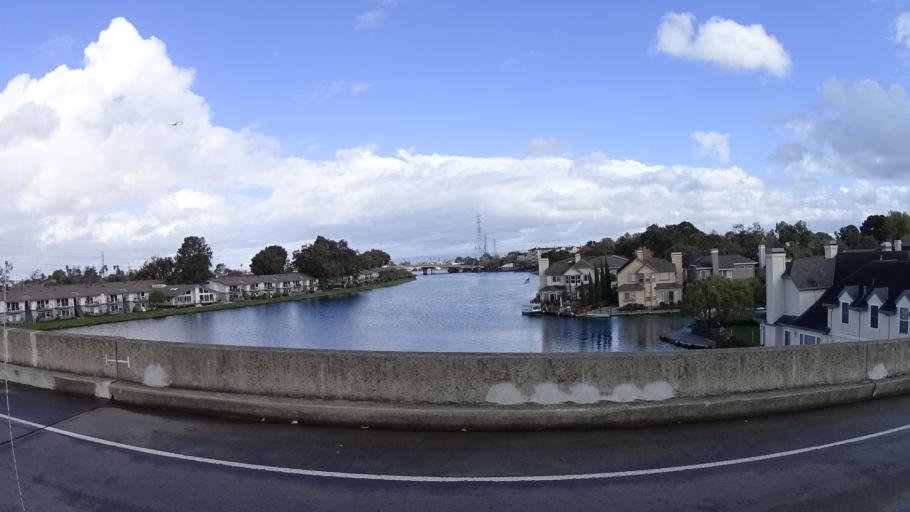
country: US
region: California
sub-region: San Mateo County
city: Foster City
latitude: 37.5534
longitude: -122.2640
